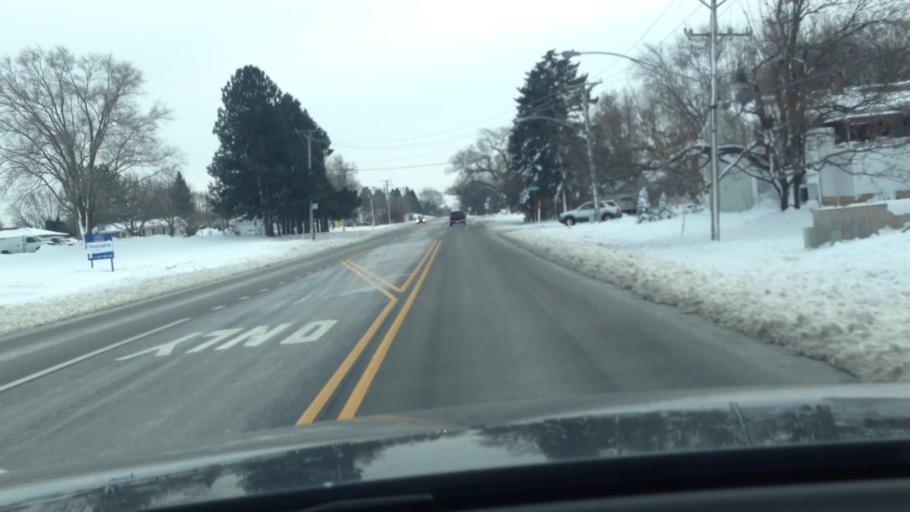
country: US
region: Illinois
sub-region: McHenry County
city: Woodstock
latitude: 42.3377
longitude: -88.4433
